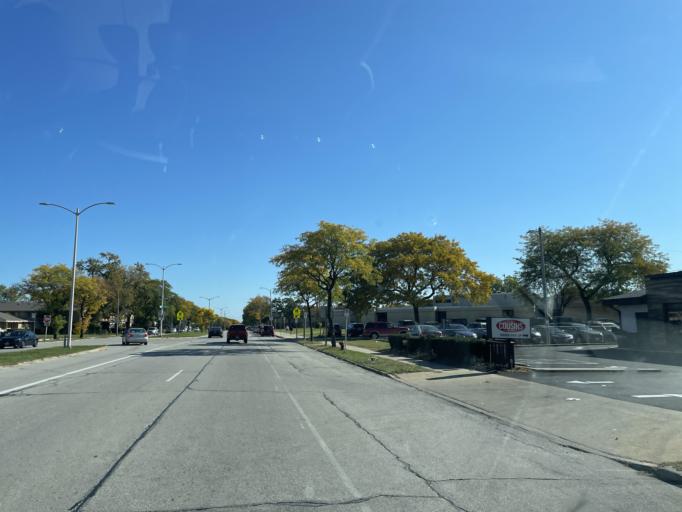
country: US
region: Wisconsin
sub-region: Waukesha County
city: Butler
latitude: 43.1119
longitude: -88.0252
